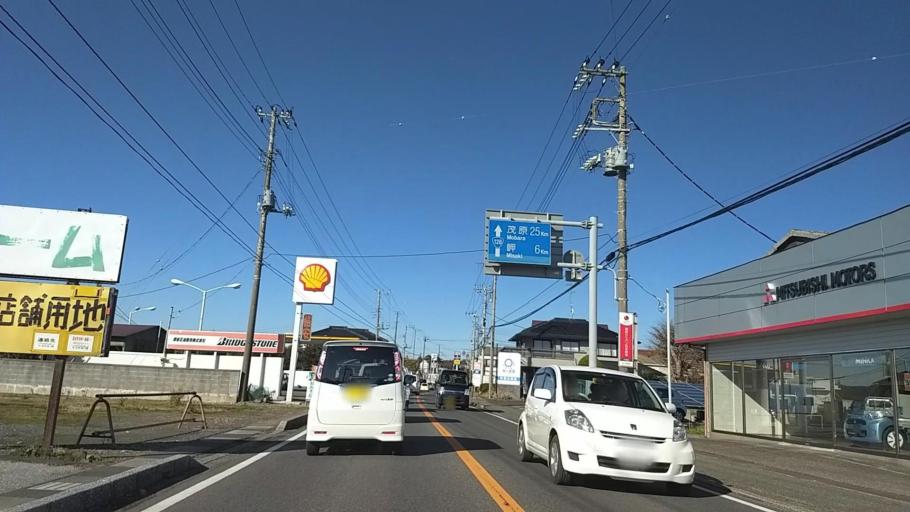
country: JP
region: Chiba
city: Ohara
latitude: 35.2566
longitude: 140.3942
